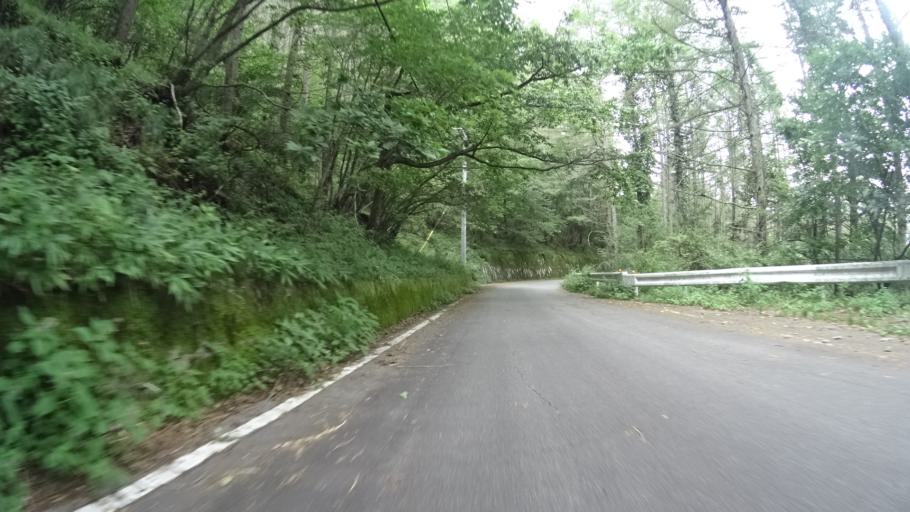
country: JP
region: Yamanashi
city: Enzan
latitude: 35.7992
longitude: 138.6404
